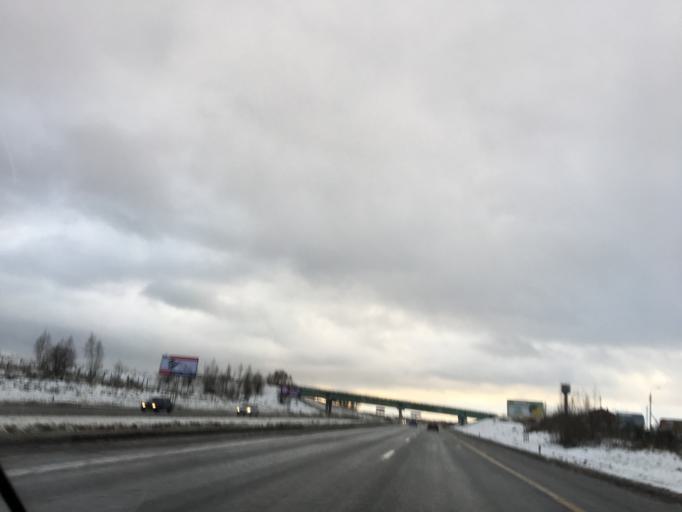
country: RU
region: Moskovskaya
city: Danki
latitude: 54.9465
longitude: 37.5300
